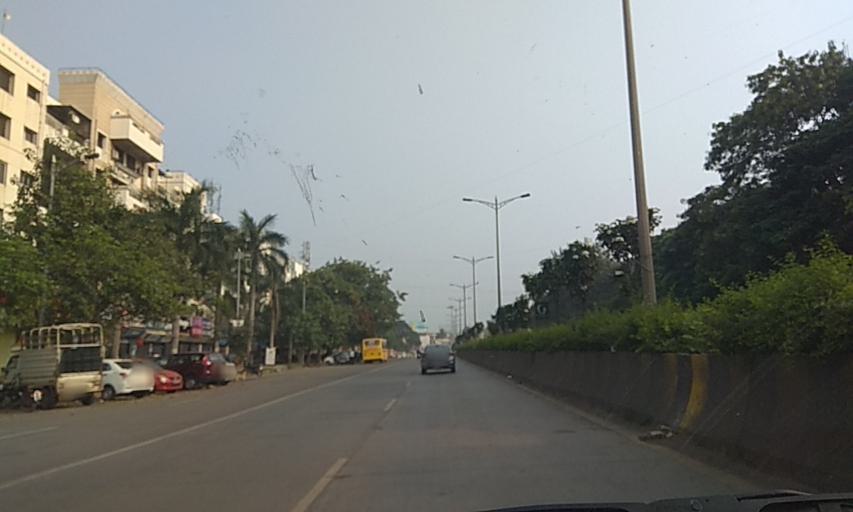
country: IN
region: Maharashtra
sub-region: Pune Division
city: Lohogaon
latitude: 18.5594
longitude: 73.9383
